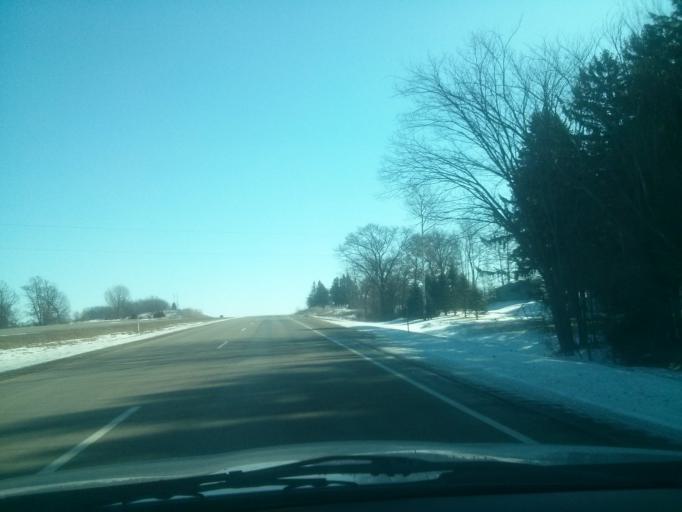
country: US
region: Wisconsin
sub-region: Saint Croix County
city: Somerset
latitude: 45.1228
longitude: -92.6242
